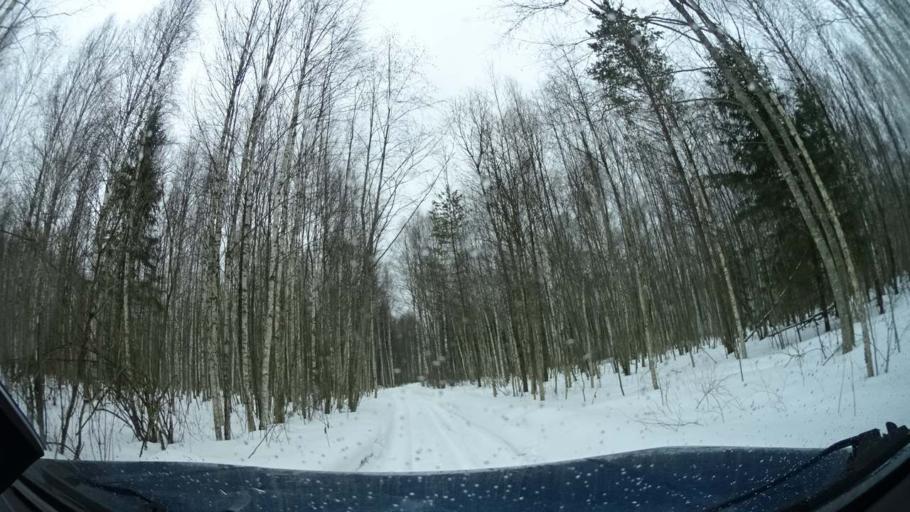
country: RU
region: Tverskaya
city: Gorodnya
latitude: 56.8030
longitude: 36.3725
